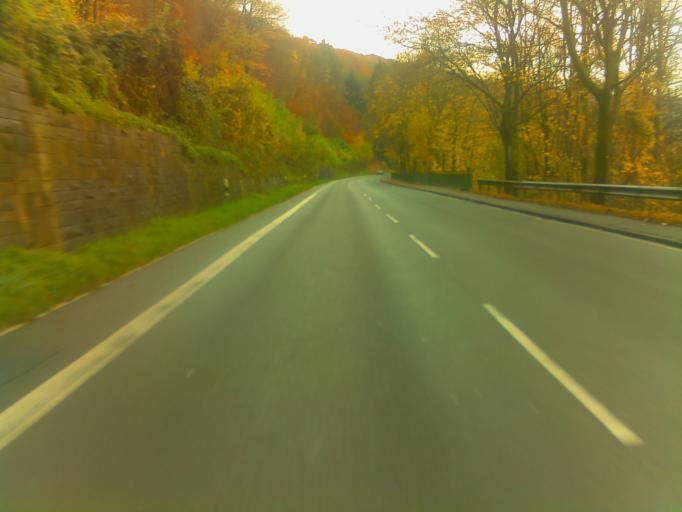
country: DE
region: Baden-Wuerttemberg
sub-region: Karlsruhe Region
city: Neckargemund
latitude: 49.4092
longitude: 8.7788
